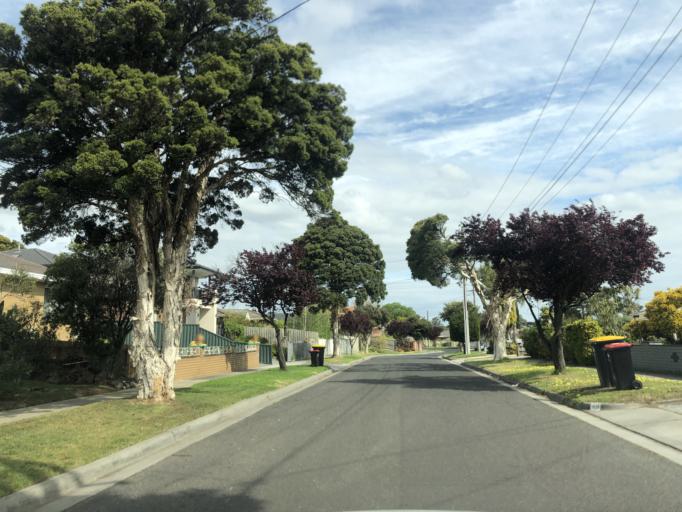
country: AU
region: Victoria
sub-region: Greater Dandenong
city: Noble Park North
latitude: -37.9512
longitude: 145.1990
